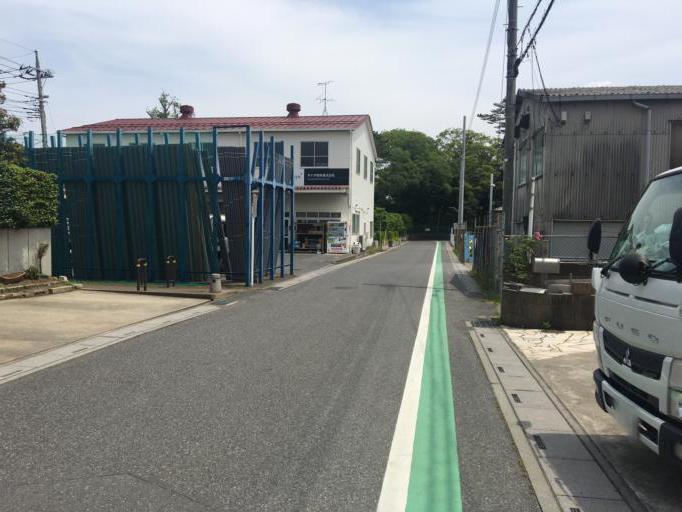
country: JP
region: Saitama
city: Koshigaya
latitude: 35.9018
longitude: 139.7888
